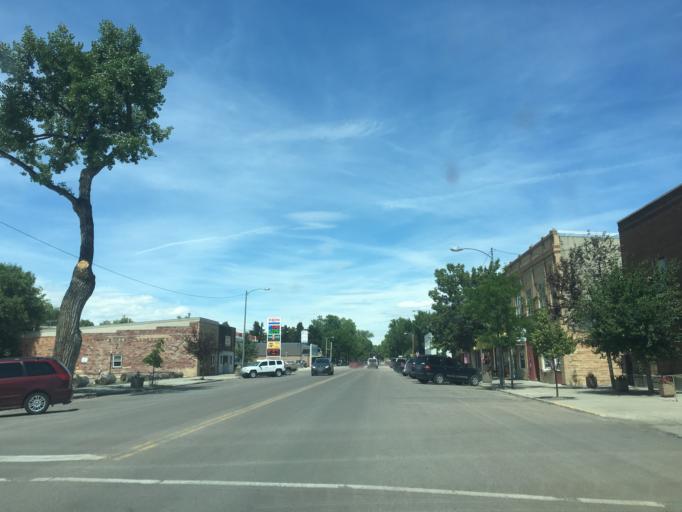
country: US
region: Montana
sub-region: Teton County
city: Choteau
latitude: 47.8129
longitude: -112.1840
